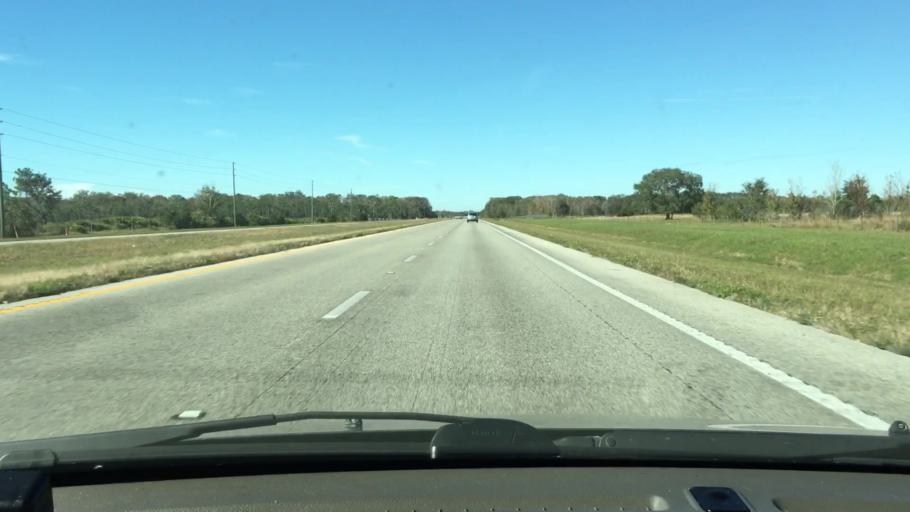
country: US
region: Florida
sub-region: Osceola County
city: Saint Cloud
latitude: 28.1293
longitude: -80.9927
